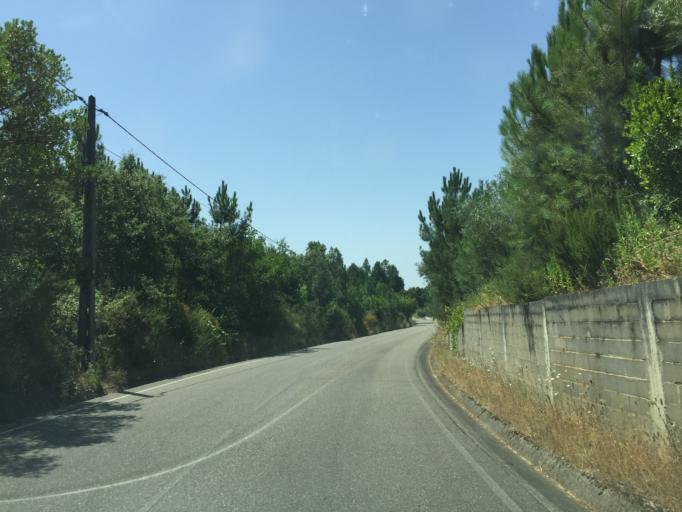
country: PT
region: Santarem
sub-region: Ferreira do Zezere
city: Ferreira do Zezere
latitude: 39.6276
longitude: -8.3092
